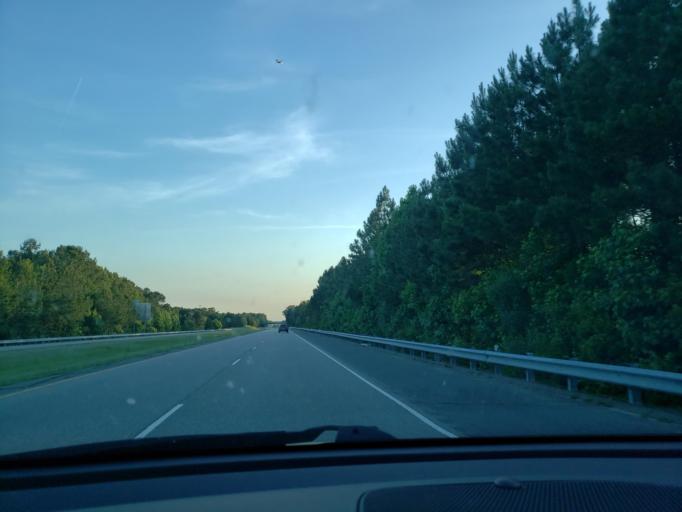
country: US
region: Virginia
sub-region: Henrico County
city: Fort Lee
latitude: 37.4766
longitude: -77.3543
